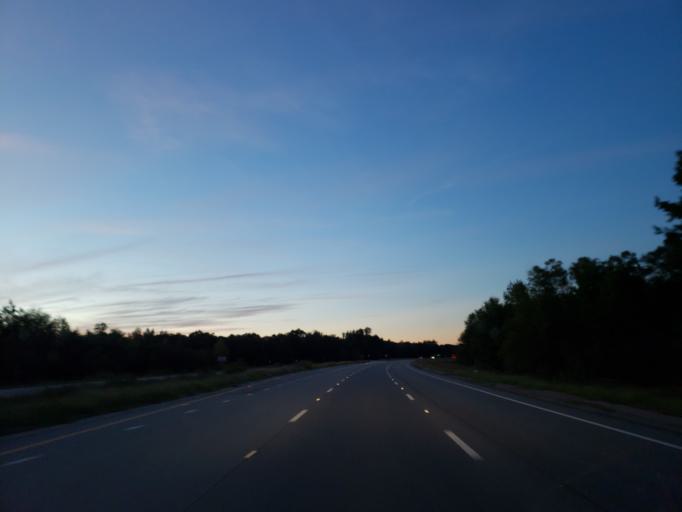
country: US
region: Mississippi
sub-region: Wayne County
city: Waynesboro
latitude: 31.8484
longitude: -88.7157
